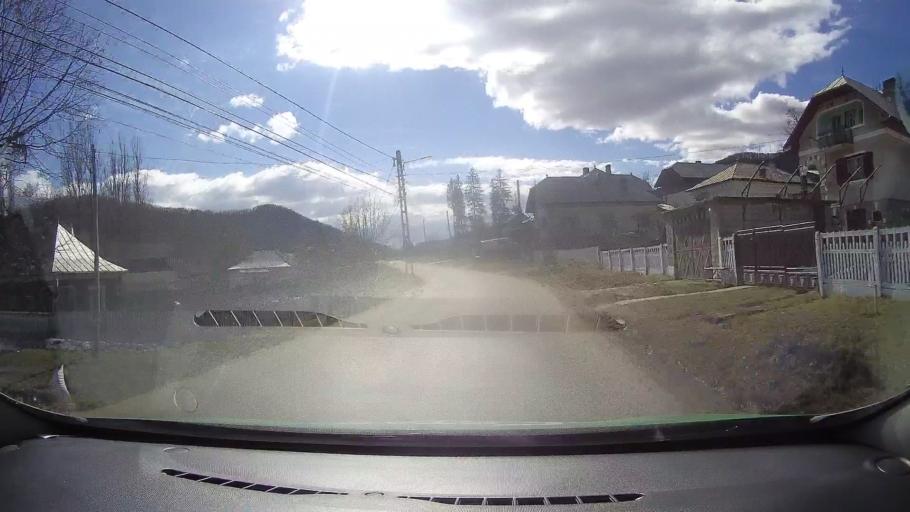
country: RO
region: Dambovita
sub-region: Comuna Vulcana Bai
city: Vulcana Bai
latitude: 45.0706
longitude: 25.3783
